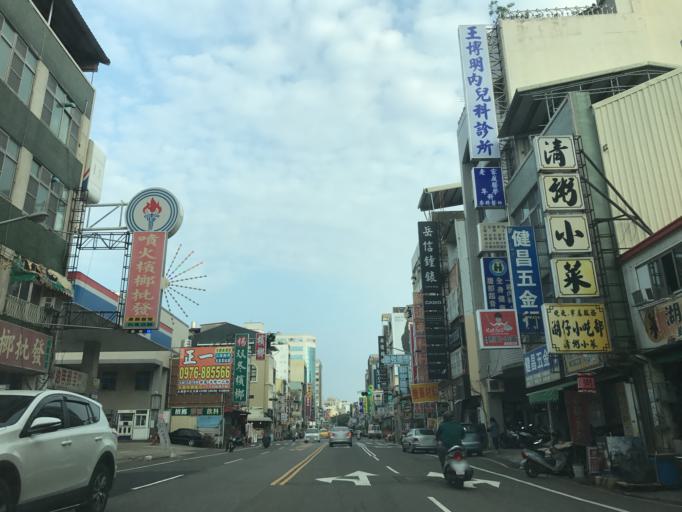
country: TW
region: Taiwan
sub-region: Tainan
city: Tainan
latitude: 22.9989
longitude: 120.1957
